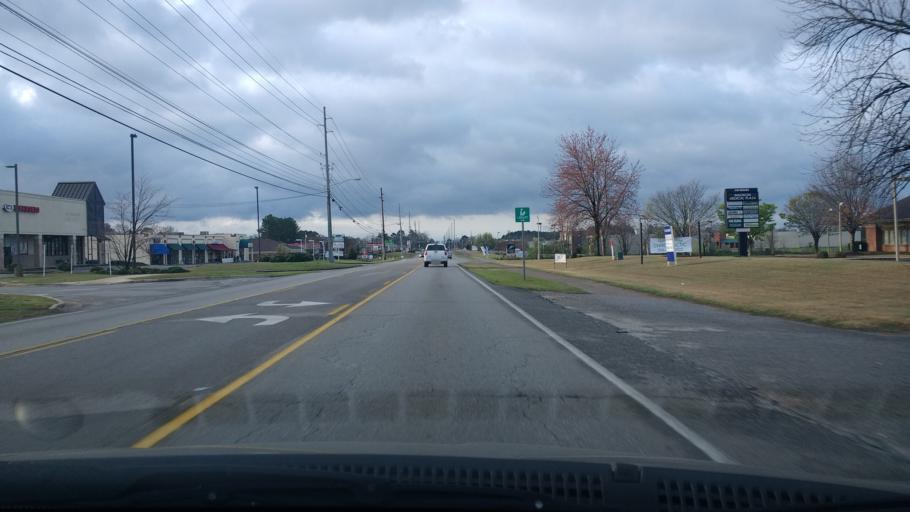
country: US
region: Alabama
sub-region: Madison County
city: Madison
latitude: 34.7112
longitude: -86.7419
